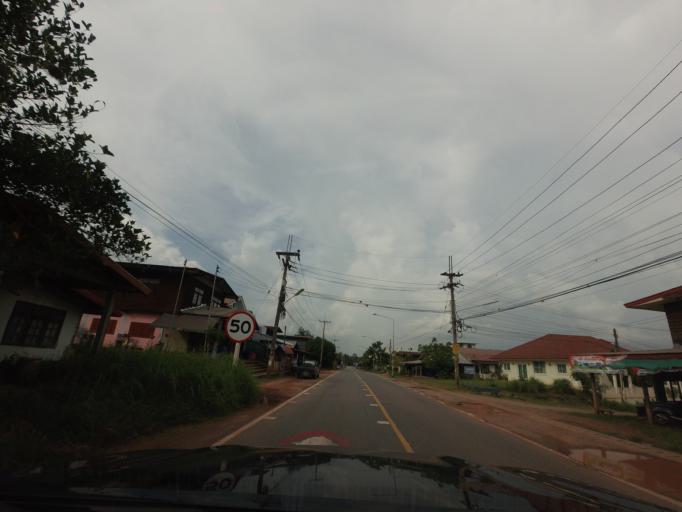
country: TH
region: Changwat Nong Bua Lamphu
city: Suwannakhuha
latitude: 17.5030
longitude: 102.3755
